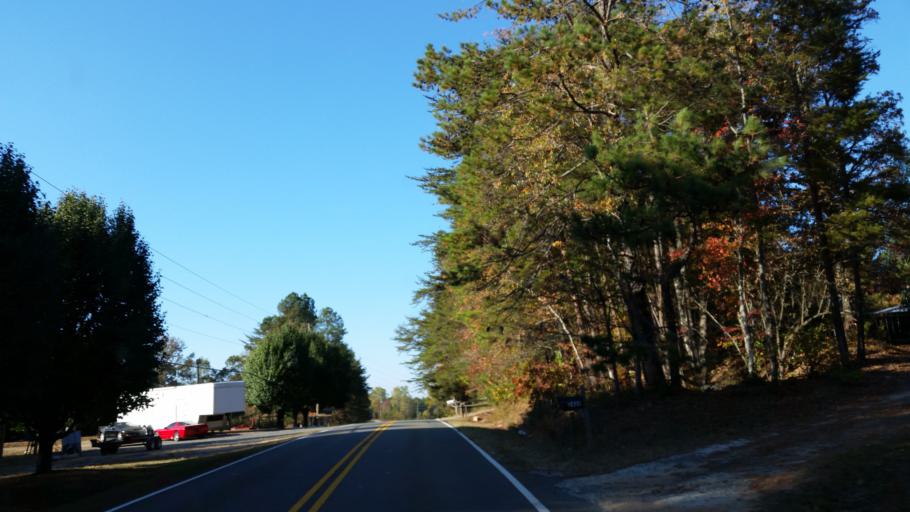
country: US
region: Georgia
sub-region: Pickens County
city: Jasper
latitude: 34.5545
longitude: -84.4696
